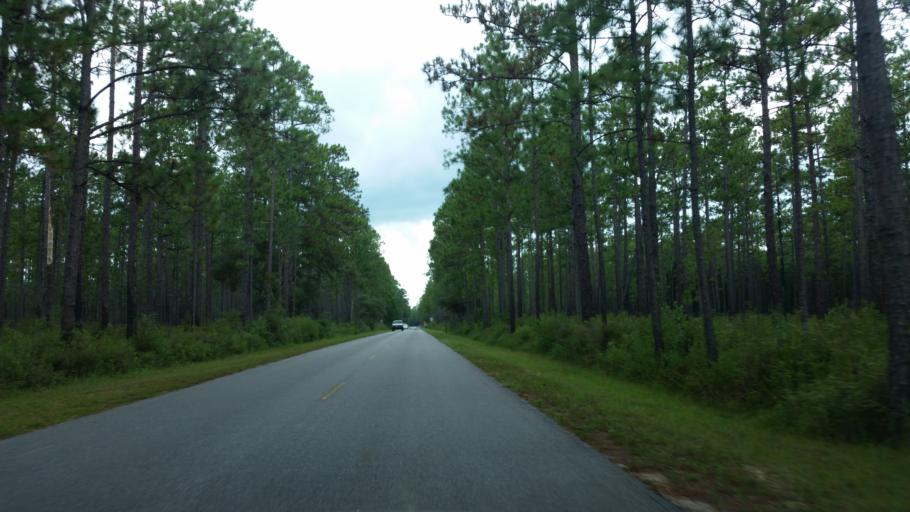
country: US
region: Florida
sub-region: Santa Rosa County
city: East Milton
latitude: 30.7152
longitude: -86.8781
